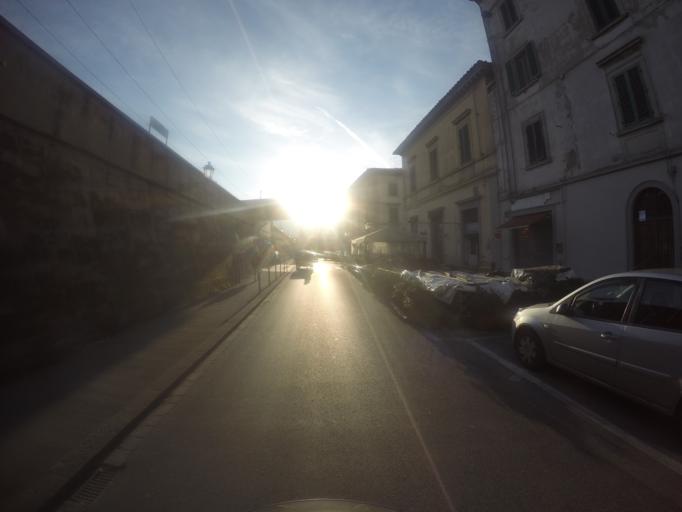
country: IT
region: Tuscany
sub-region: Provincia di Prato
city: Prato
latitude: 43.8845
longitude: 11.0978
